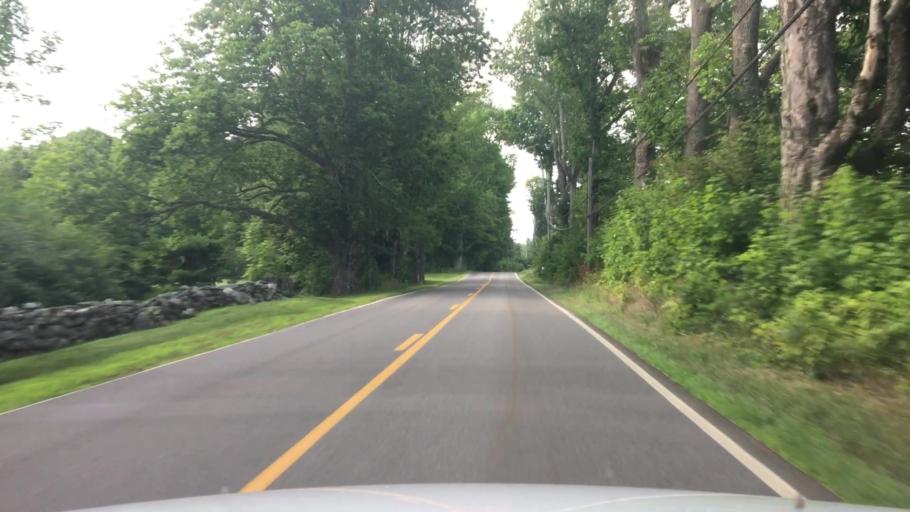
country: US
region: Maine
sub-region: Lincoln County
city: Waldoboro
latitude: 44.1351
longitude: -69.3705
